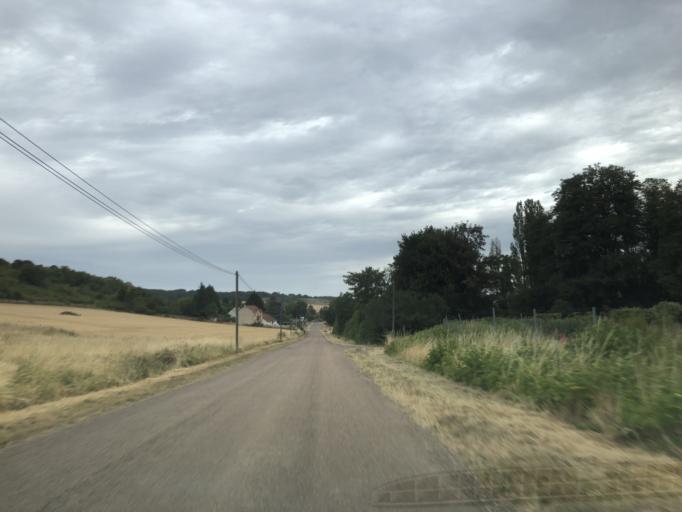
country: FR
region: Bourgogne
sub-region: Departement de l'Yonne
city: Aillant-sur-Tholon
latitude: 47.9120
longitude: 3.3222
